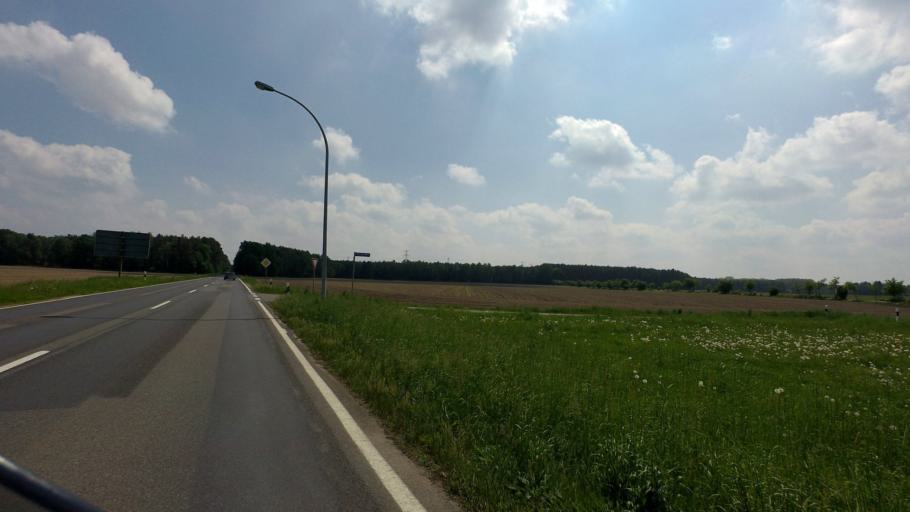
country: DE
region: Saxony
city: Schleife
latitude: 51.5703
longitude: 14.4768
